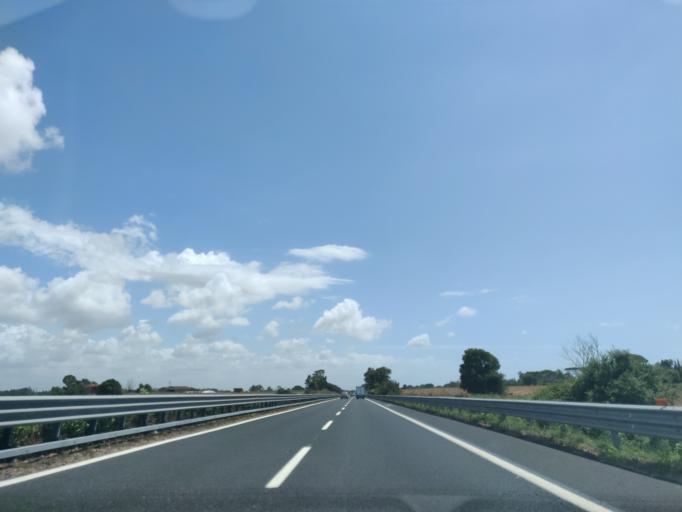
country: IT
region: Latium
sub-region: Citta metropolitana di Roma Capitale
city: Maccarese
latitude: 41.8491
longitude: 12.2692
